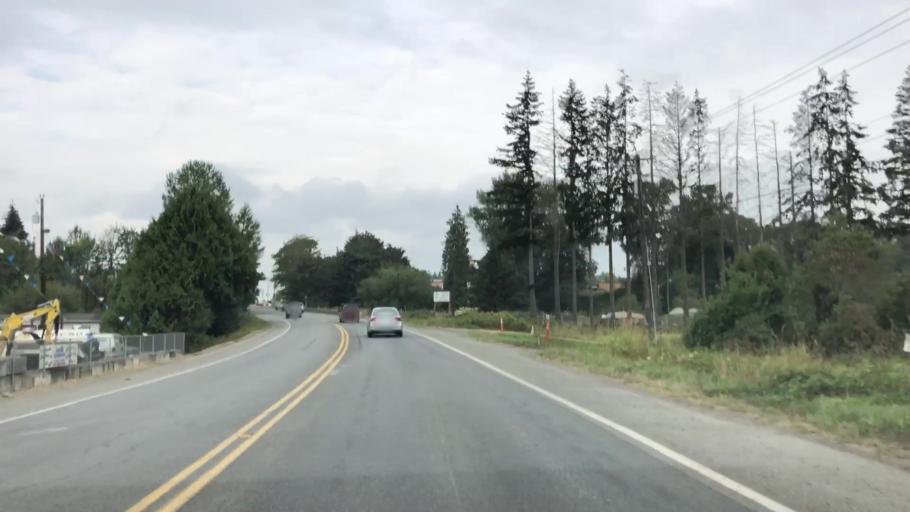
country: US
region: Washington
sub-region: Snohomish County
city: Snohomish
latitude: 47.9133
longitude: -122.0806
